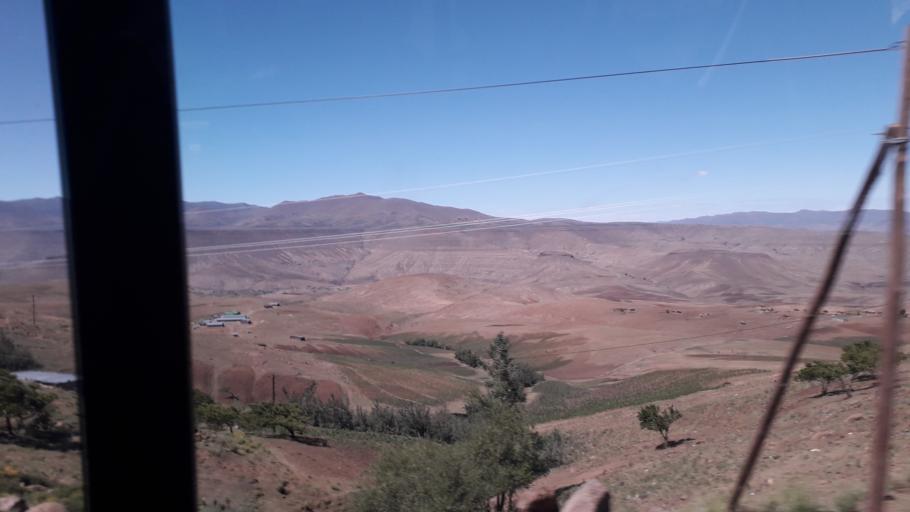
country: LS
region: Mokhotlong
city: Mokhotlong
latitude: -29.2807
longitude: 28.9443
